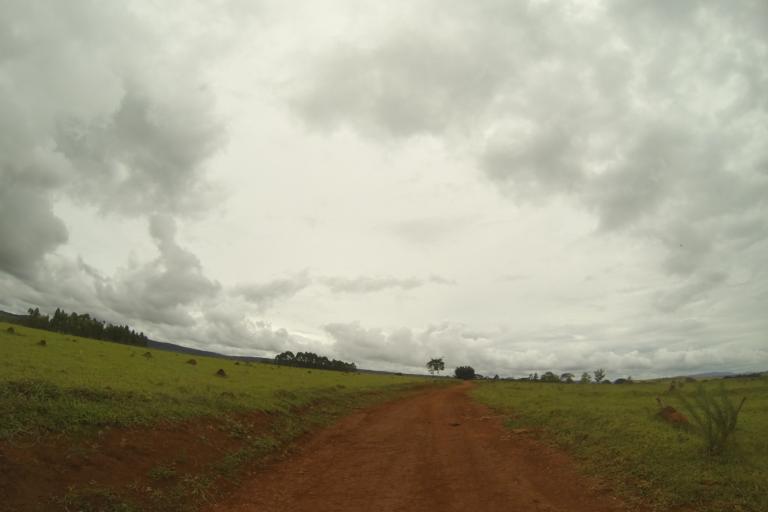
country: BR
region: Minas Gerais
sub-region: Ibia
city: Ibia
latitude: -19.7313
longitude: -46.6034
